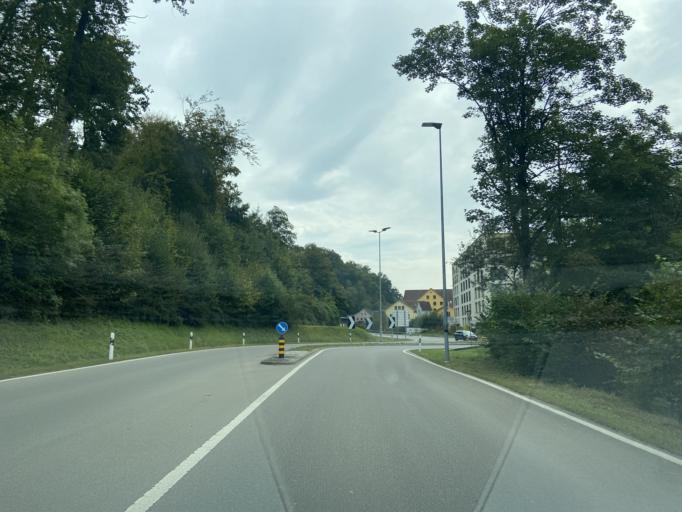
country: CH
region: Zurich
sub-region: Bezirk Pfaeffikon
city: Effretikon / Watt
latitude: 47.4328
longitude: 8.7042
